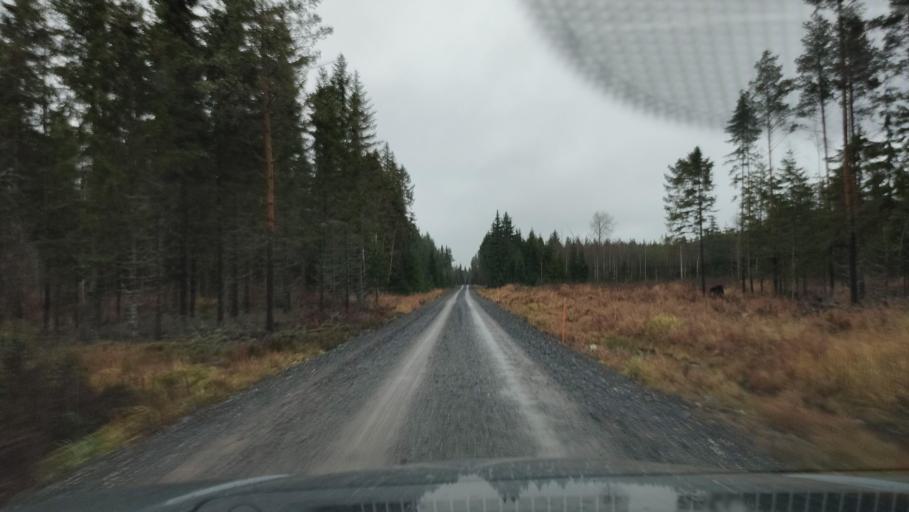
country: FI
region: Southern Ostrobothnia
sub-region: Suupohja
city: Karijoki
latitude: 62.1639
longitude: 21.6091
